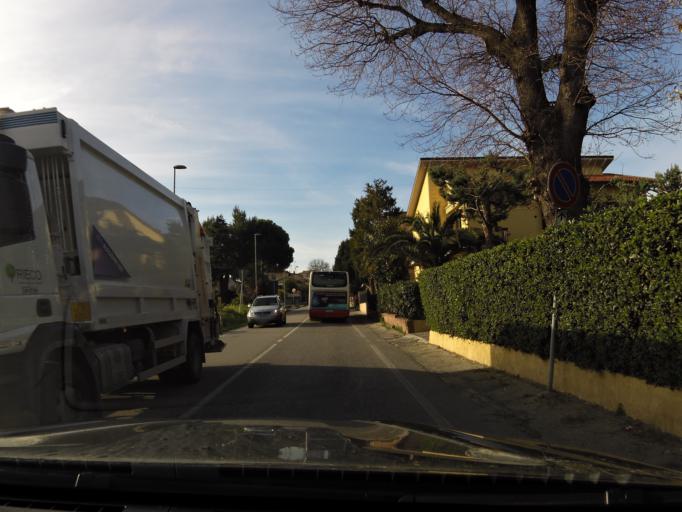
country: IT
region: The Marches
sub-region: Provincia di Ancona
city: Villa Musone
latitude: 43.4589
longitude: 13.5826
